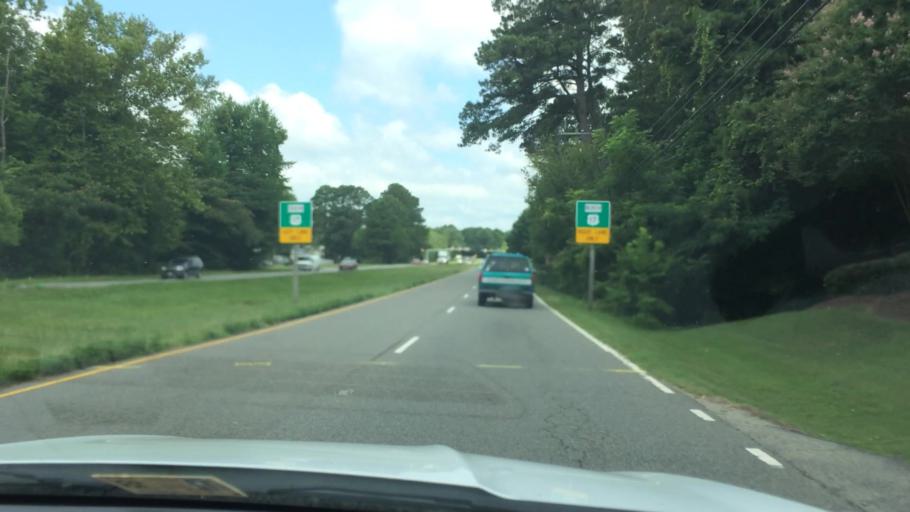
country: US
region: Virginia
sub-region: City of Poquoson
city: Poquoson
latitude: 37.1225
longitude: -76.4533
